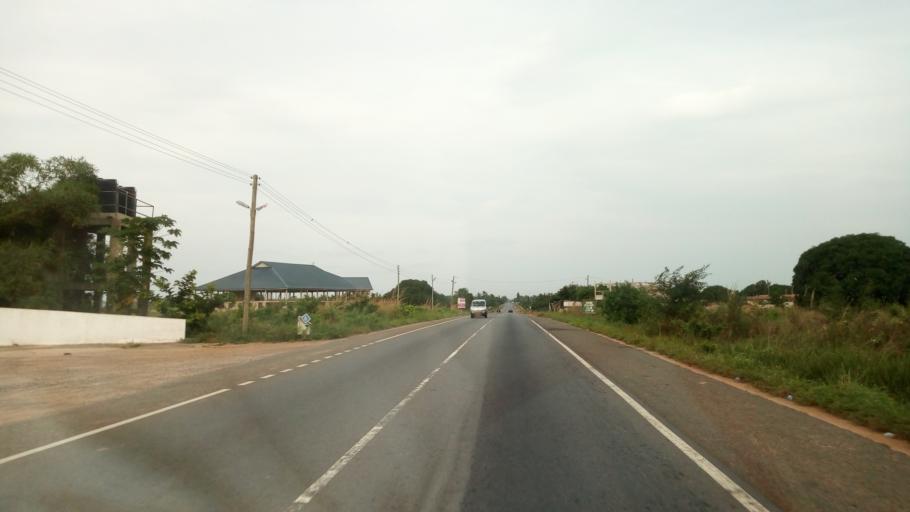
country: GH
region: Volta
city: Keta
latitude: 6.0570
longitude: 0.9878
